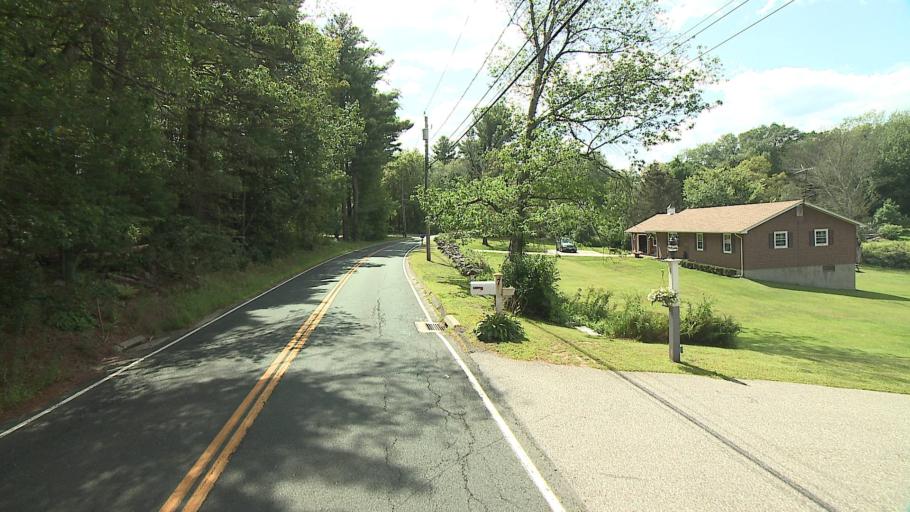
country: US
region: Connecticut
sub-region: Tolland County
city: Stafford Springs
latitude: 41.9520
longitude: -72.3271
